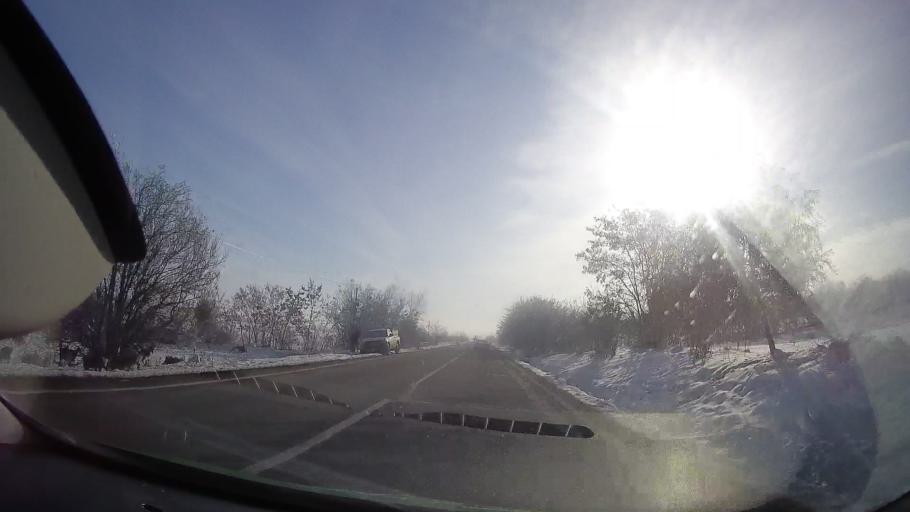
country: RO
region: Neamt
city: Bodesti
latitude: 47.0105
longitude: 26.4243
